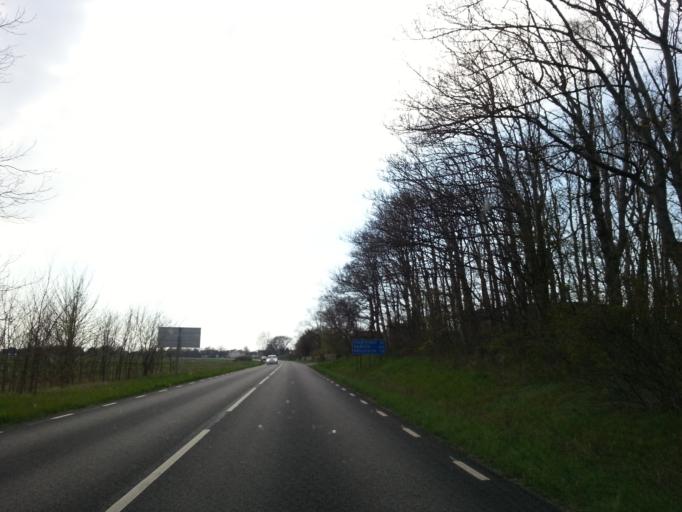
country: SE
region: Skane
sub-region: Trelleborgs Kommun
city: Skare
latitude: 55.3767
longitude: 13.0932
